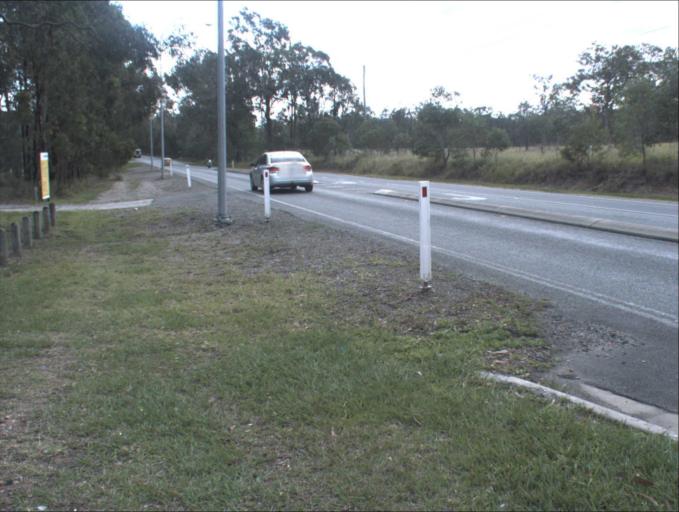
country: AU
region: Queensland
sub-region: Logan
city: North Maclean
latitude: -27.7362
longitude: 152.9846
